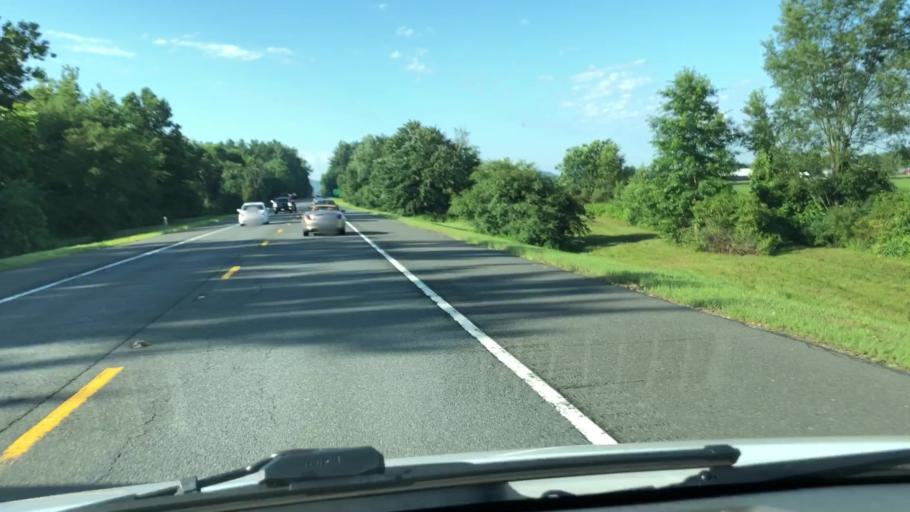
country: US
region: Massachusetts
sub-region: Hampshire County
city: North Amherst
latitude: 42.4045
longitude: -72.5386
